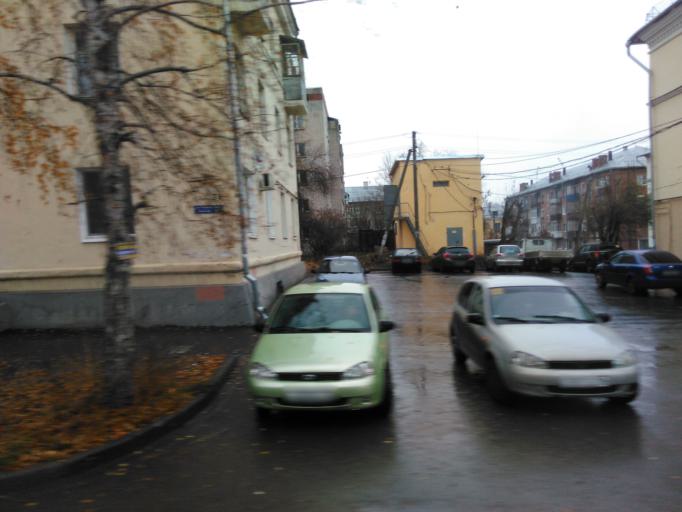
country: RU
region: Tatarstan
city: Osinovo
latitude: 55.8209
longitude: 48.8989
